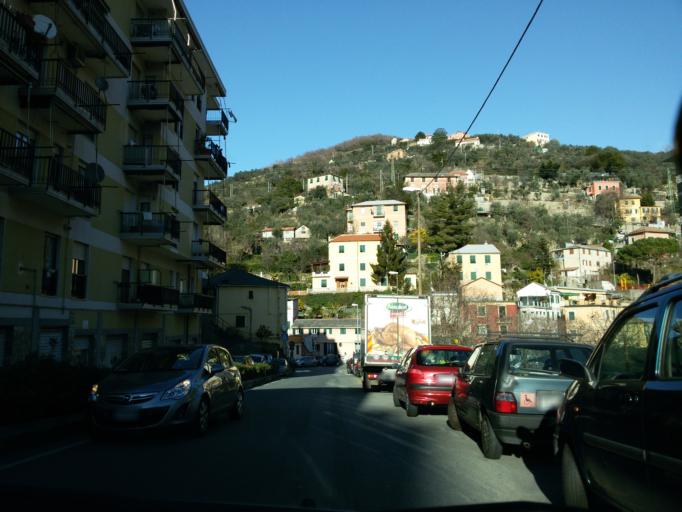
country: IT
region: Liguria
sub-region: Provincia di Genova
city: Piccarello
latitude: 44.4250
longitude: 8.9781
